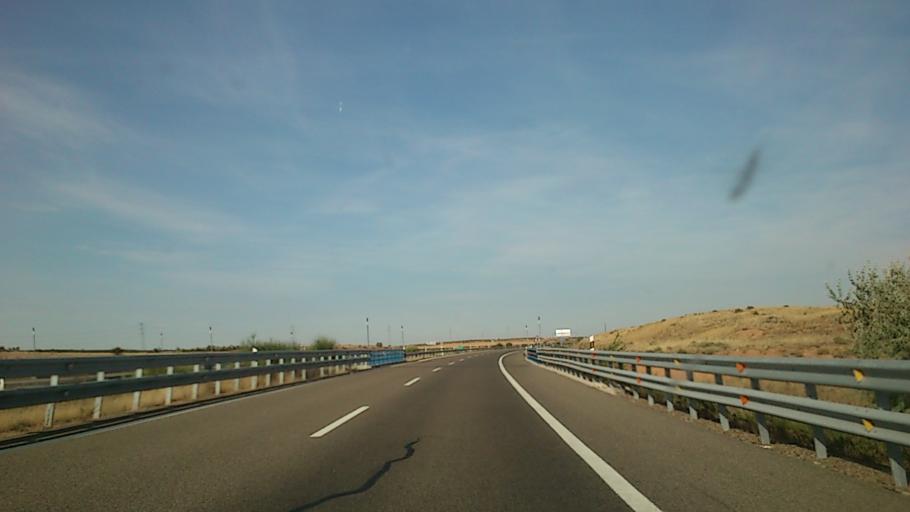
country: ES
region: Aragon
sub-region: Provincia de Zaragoza
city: Longares
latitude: 41.4079
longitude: -1.1750
